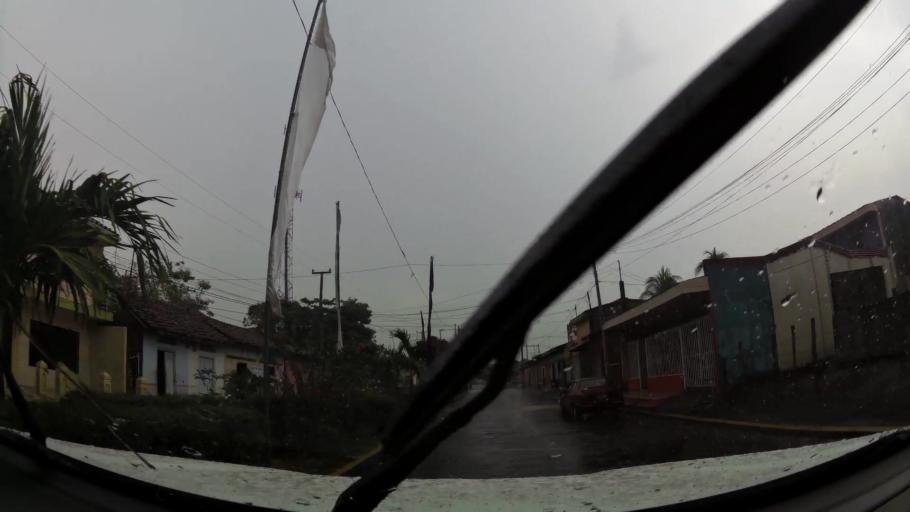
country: NI
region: Leon
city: Telica
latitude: 12.5215
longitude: -86.8615
